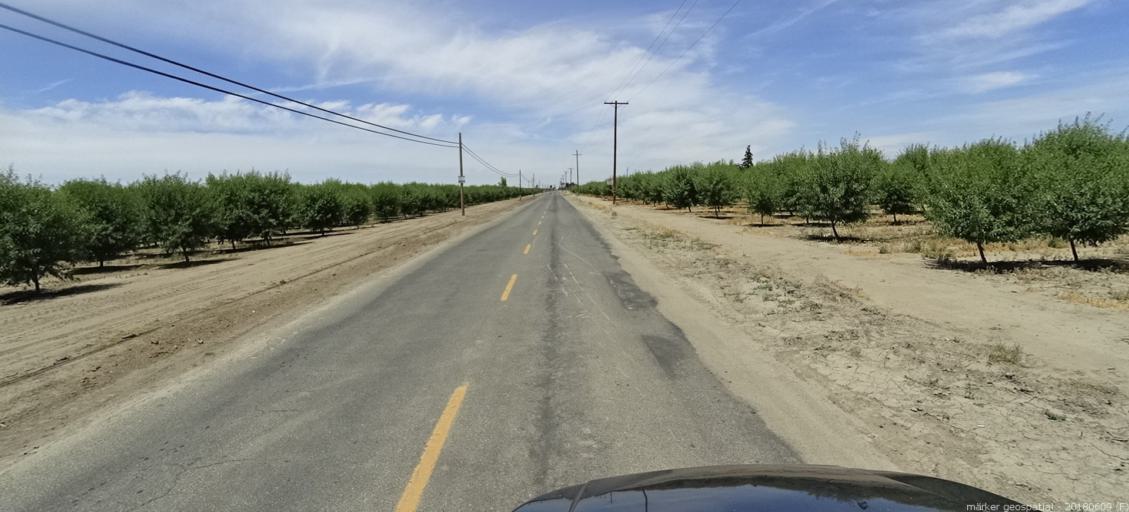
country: US
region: California
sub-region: Madera County
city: Parkwood
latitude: 36.8903
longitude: -120.0923
